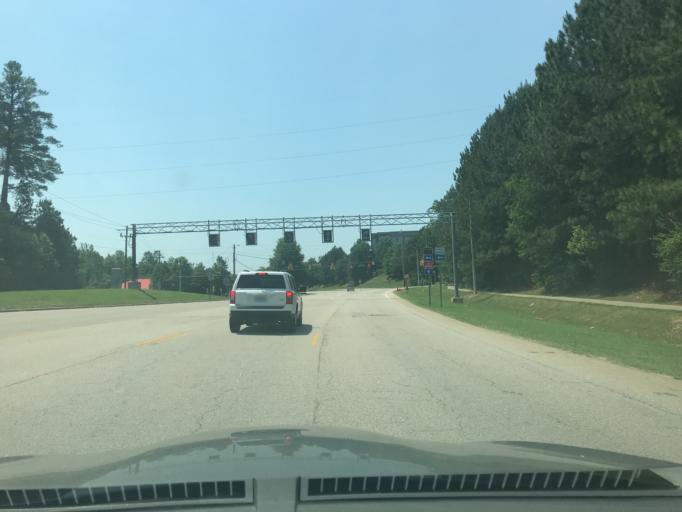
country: US
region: North Carolina
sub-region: Wake County
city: Cary
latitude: 35.8012
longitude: -78.7269
